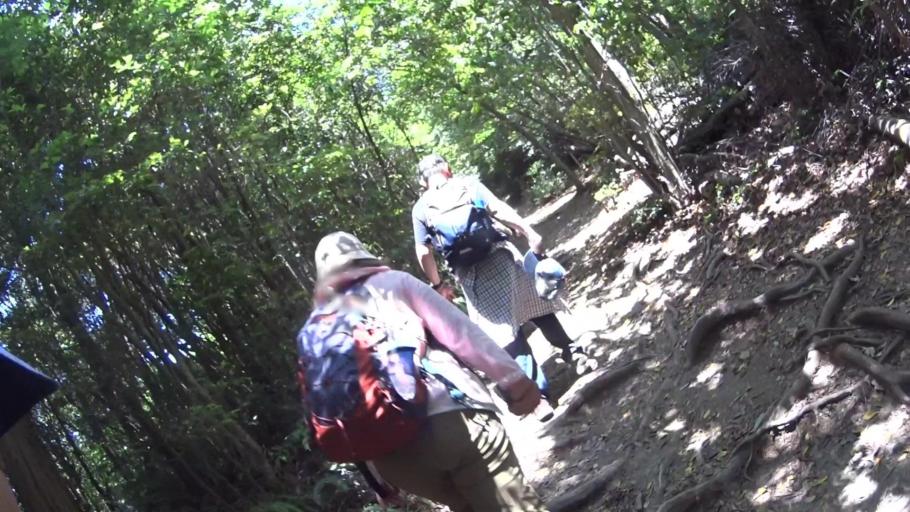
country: JP
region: Kyoto
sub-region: Kyoto-shi
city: Kamigyo-ku
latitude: 35.0152
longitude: 135.8068
